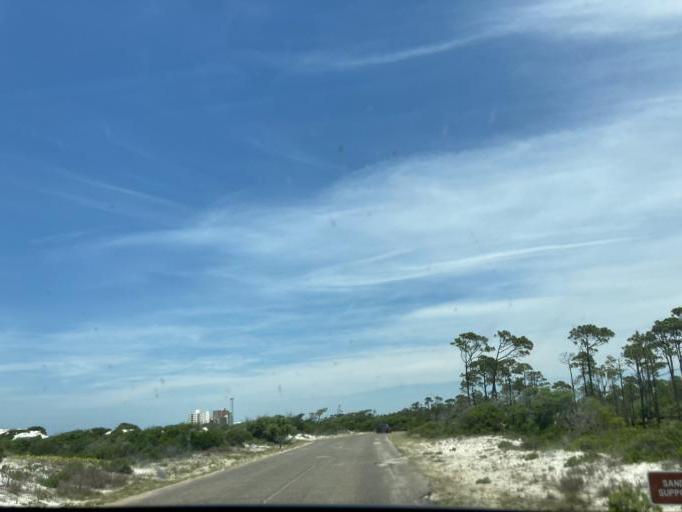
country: US
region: Florida
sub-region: Bay County
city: Lower Grand Lagoon
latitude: 30.1285
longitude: -85.7374
